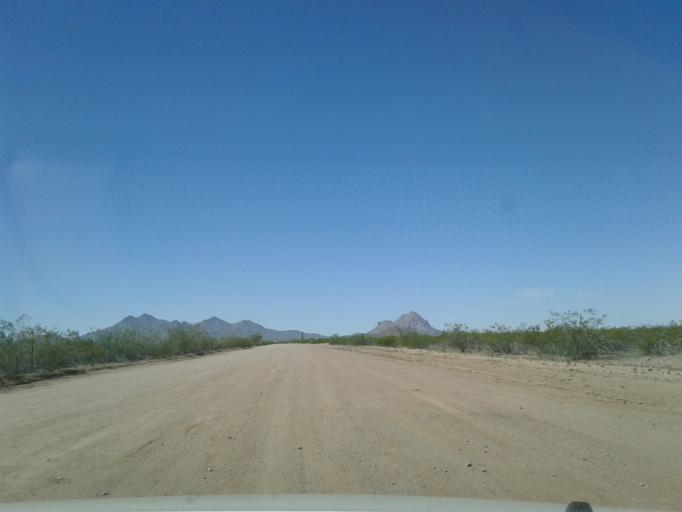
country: US
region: Arizona
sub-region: Pima County
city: Avra Valley
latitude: 32.4293
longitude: -111.3730
